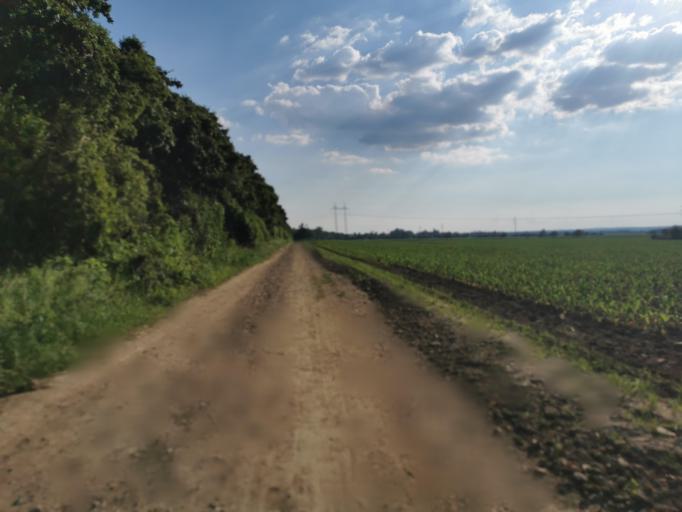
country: CZ
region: South Moravian
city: Straznice
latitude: 48.8855
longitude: 17.3253
